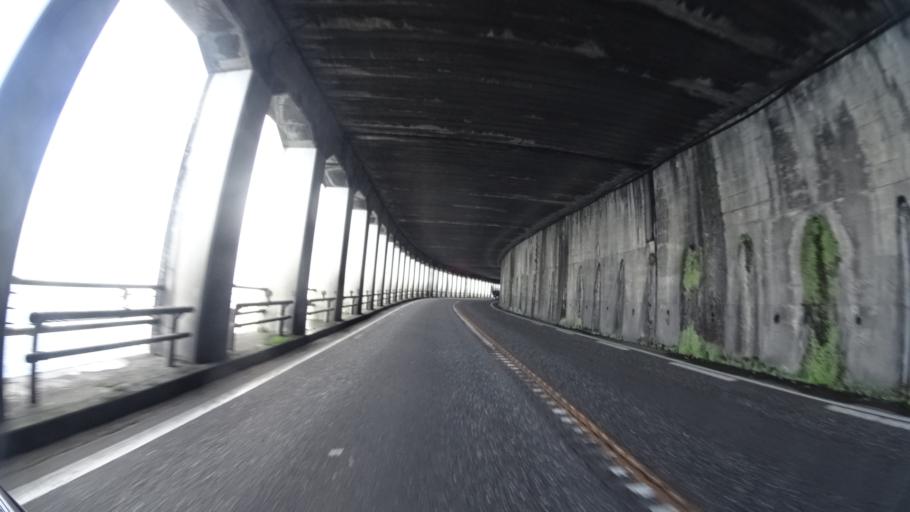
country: JP
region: Niigata
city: Itoigawa
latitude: 36.9901
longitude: 137.6809
